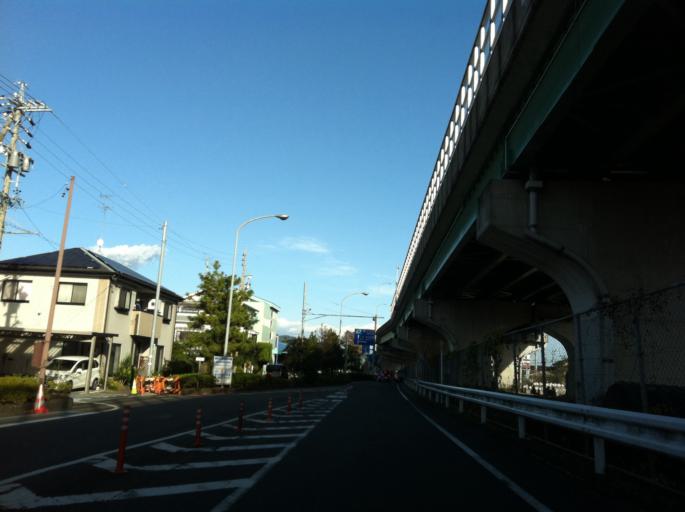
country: JP
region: Shizuoka
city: Shizuoka-shi
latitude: 35.0170
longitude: 138.4421
